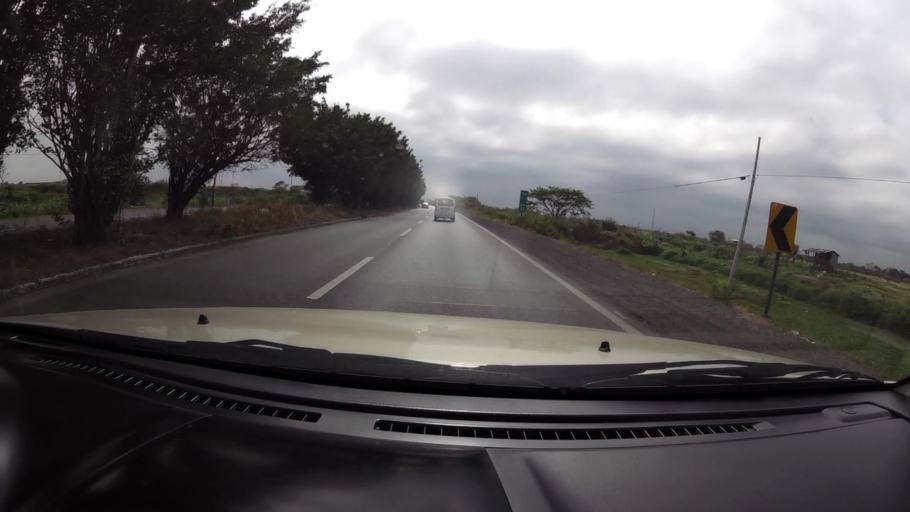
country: EC
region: Guayas
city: Yaguachi Nuevo
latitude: -2.2087
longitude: -79.7381
